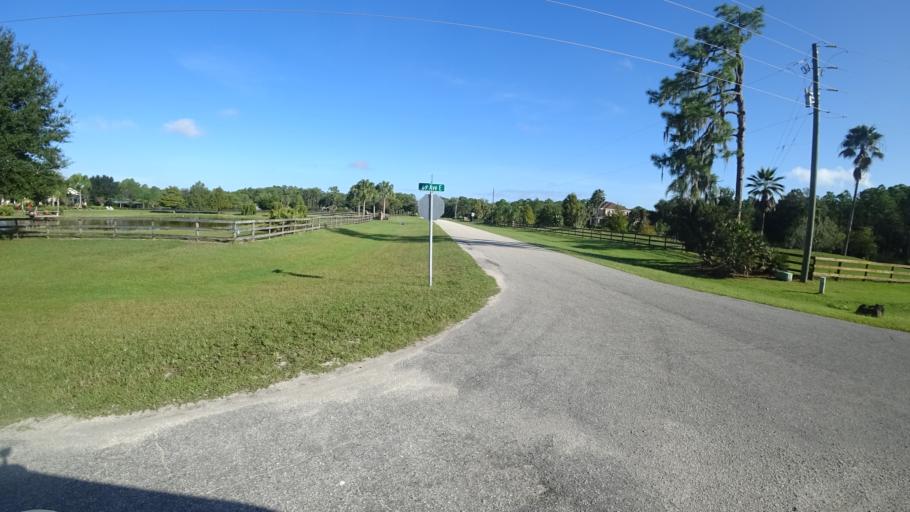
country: US
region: Florida
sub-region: Sarasota County
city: The Meadows
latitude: 27.4172
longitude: -82.3438
